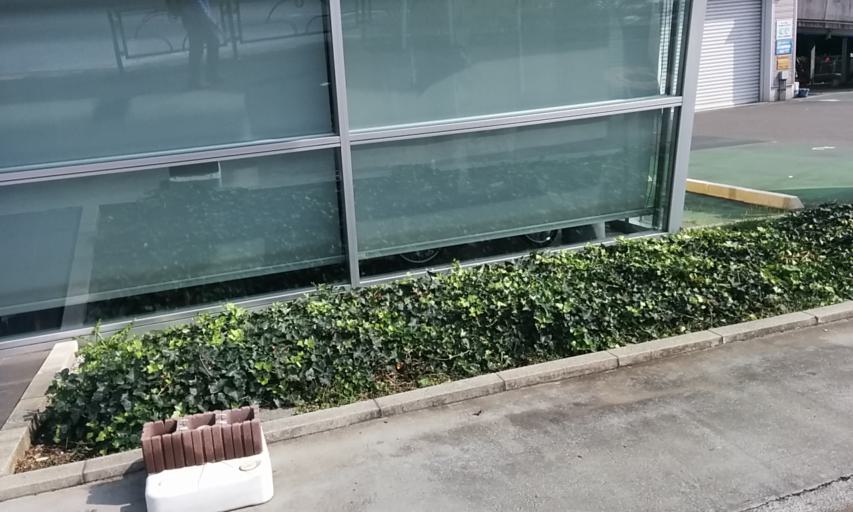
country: JP
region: Tokyo
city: Kokubunji
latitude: 35.6892
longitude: 139.4693
